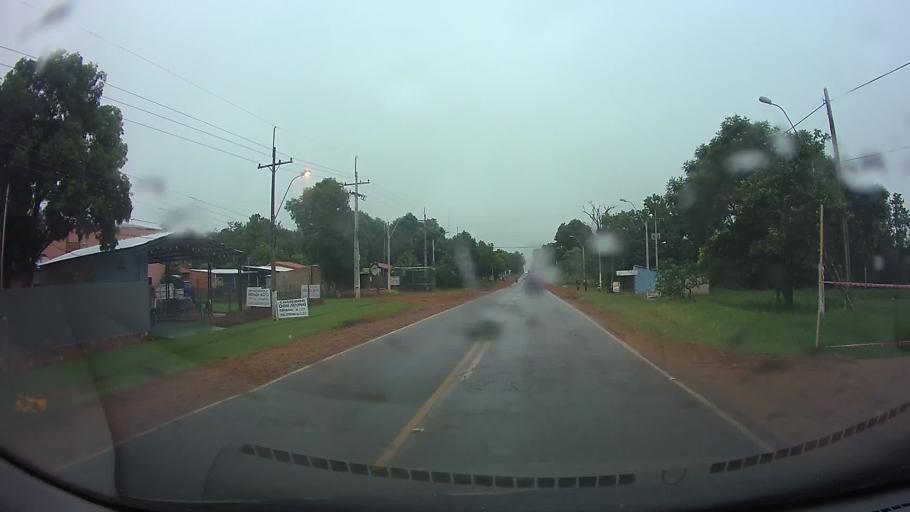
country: PY
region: Central
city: Ita
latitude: -25.4653
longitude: -57.3654
